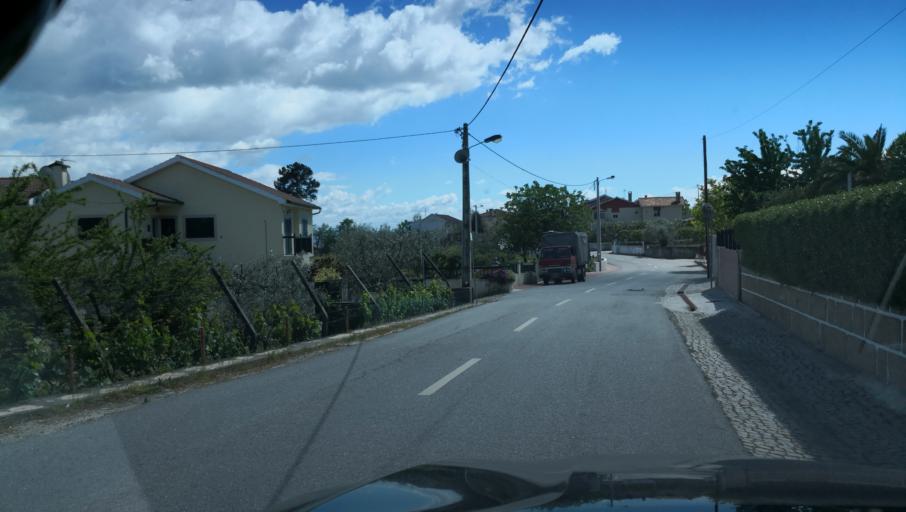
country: PT
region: Vila Real
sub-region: Vila Real
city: Vila Real
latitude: 41.2607
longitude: -7.7322
